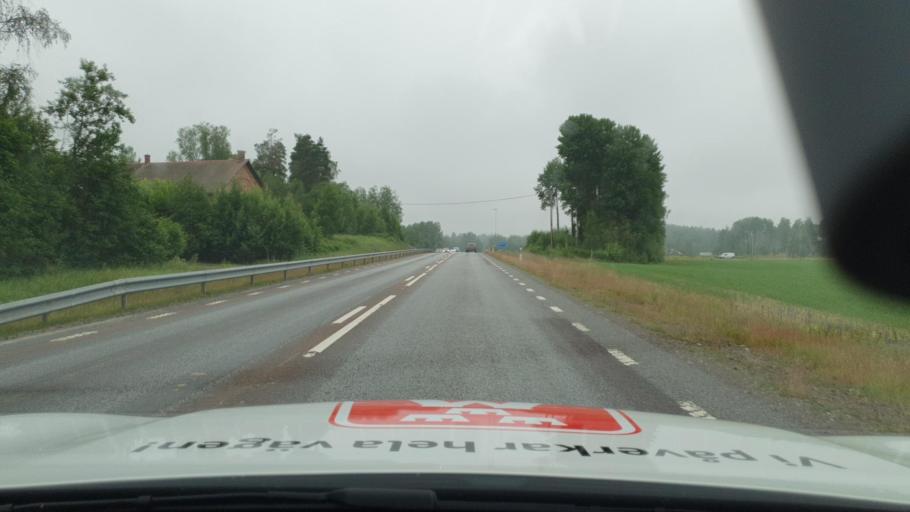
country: SE
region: Vaermland
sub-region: Karlstads Kommun
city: Edsvalla
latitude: 59.5754
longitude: 13.1756
